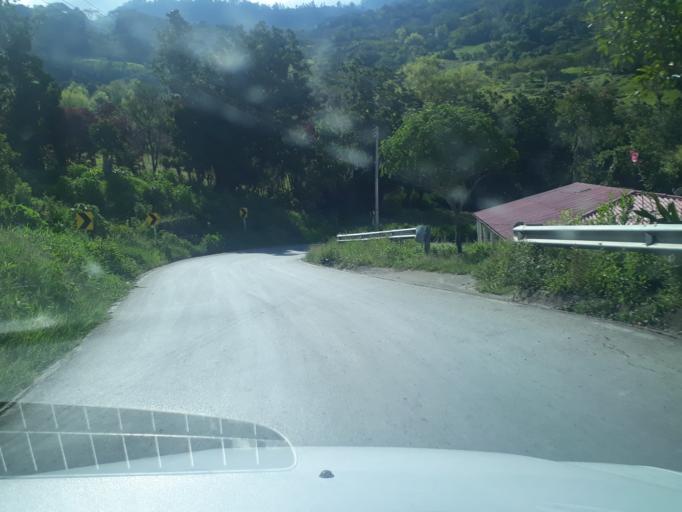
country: CO
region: Santander
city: Velez
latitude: 6.0450
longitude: -73.6523
